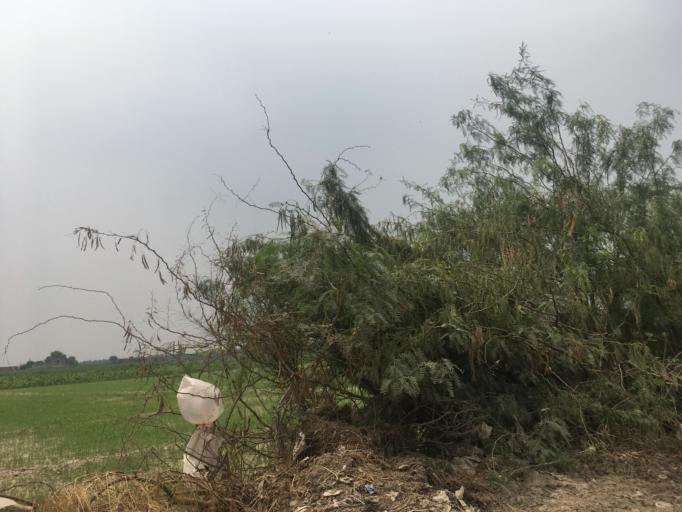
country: PK
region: Punjab
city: Lahore
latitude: 31.6224
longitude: 74.3469
